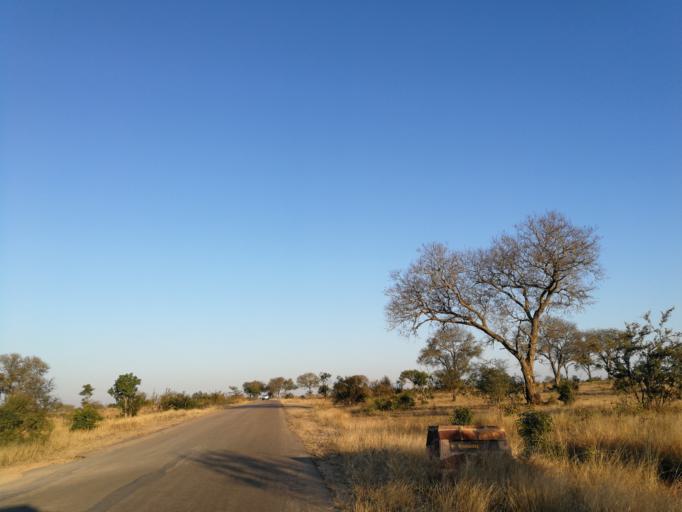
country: ZA
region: Limpopo
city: Thulamahashi
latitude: -25.0231
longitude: 31.3339
